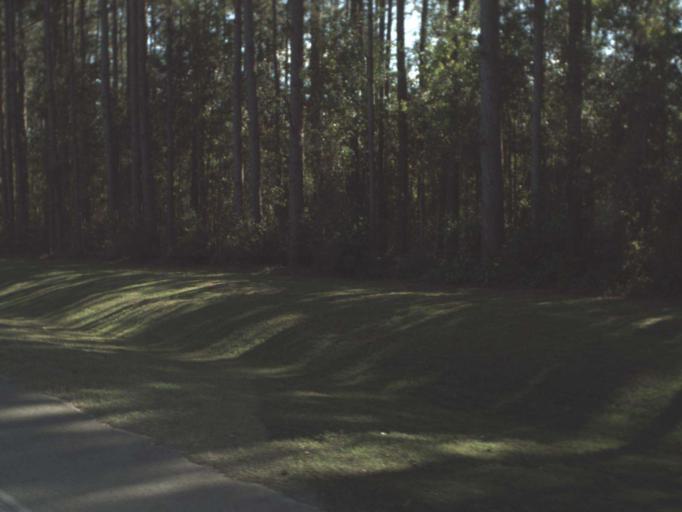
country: US
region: Florida
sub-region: Gulf County
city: Wewahitchka
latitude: 30.0933
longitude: -85.1964
